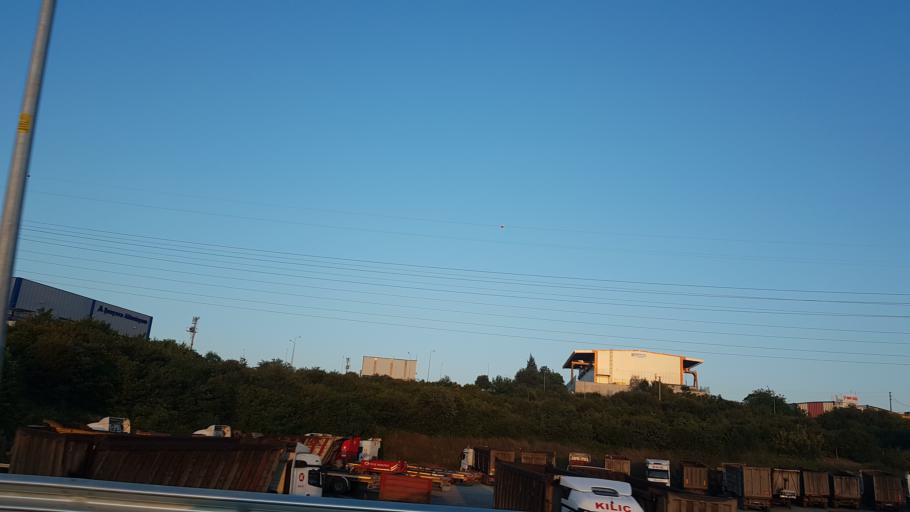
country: TR
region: Kocaeli
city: Tavsanli
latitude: 40.8074
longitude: 29.5197
